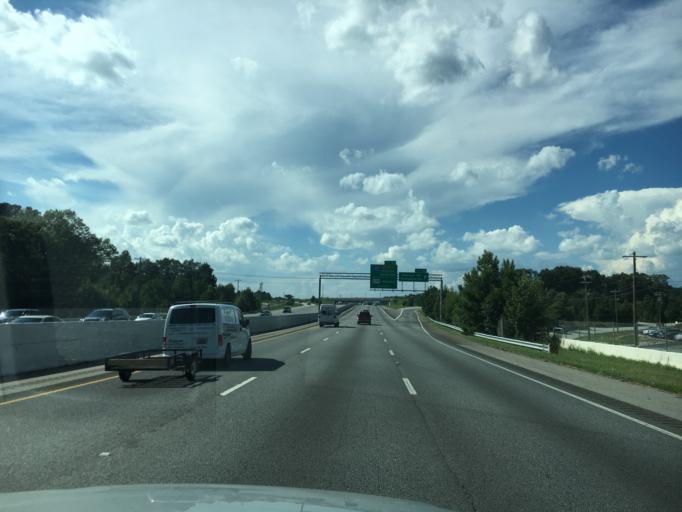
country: US
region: South Carolina
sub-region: Greenville County
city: Simpsonville
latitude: 34.7330
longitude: -82.2676
